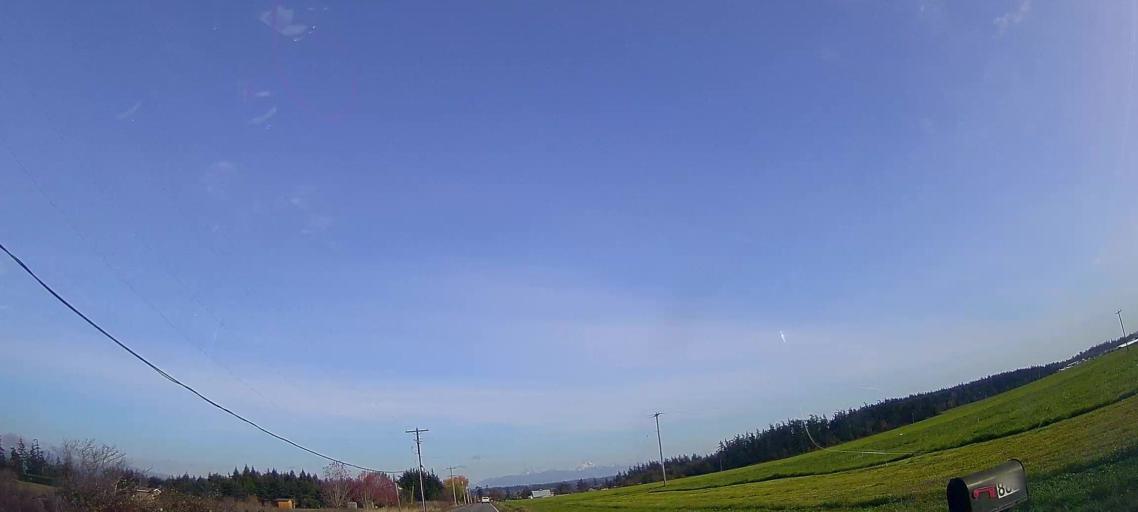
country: US
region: Washington
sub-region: Snohomish County
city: Stanwood
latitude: 48.2544
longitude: -122.4344
